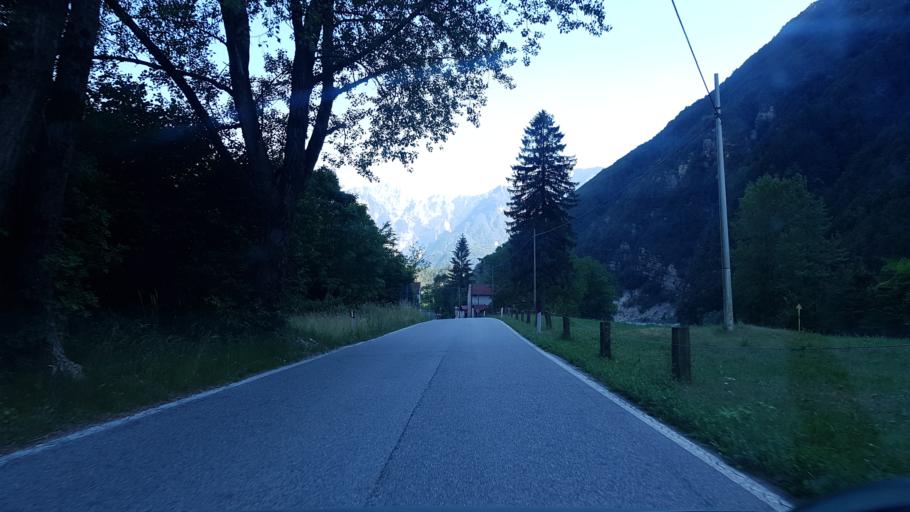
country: IT
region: Friuli Venezia Giulia
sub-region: Provincia di Udine
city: Moggio Udinese
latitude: 46.4347
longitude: 13.1988
